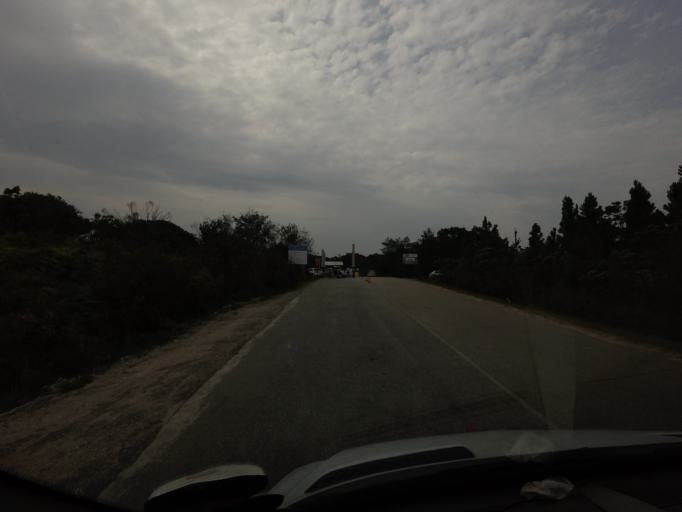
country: ZA
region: Eastern Cape
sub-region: Cacadu District Municipality
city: Kareedouw
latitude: -34.0100
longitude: 23.8679
